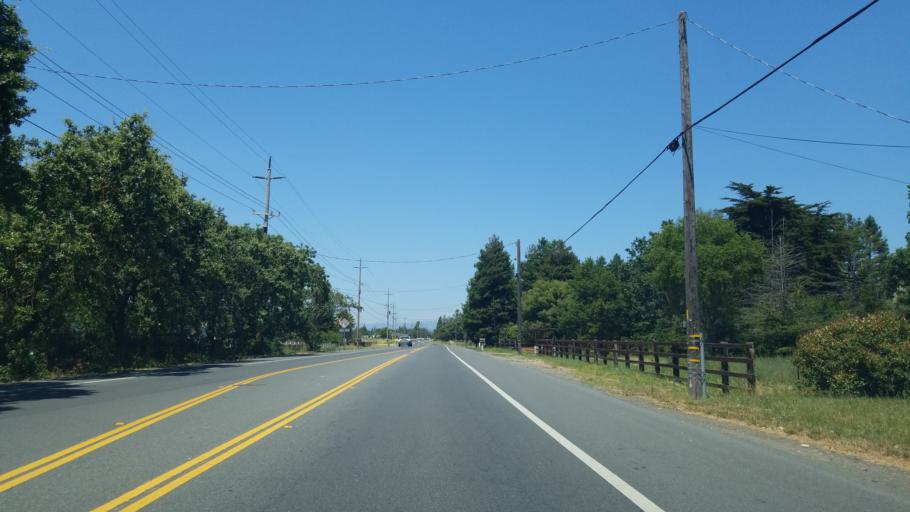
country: US
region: California
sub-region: Sonoma County
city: Roseland
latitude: 38.3779
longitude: -122.7415
